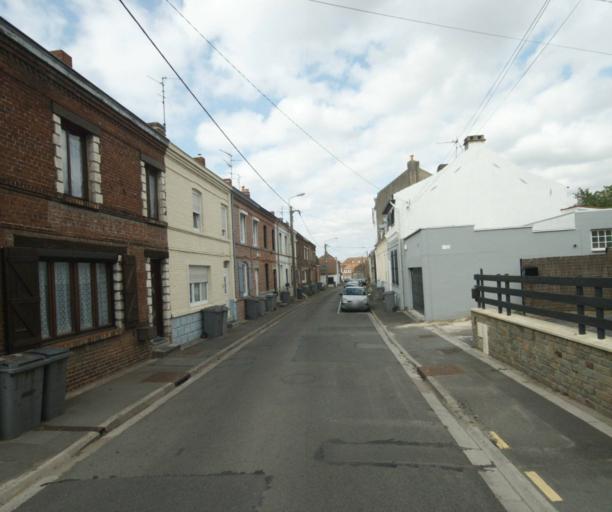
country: FR
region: Nord-Pas-de-Calais
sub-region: Departement du Nord
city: Chereng
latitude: 50.6090
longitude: 3.2085
